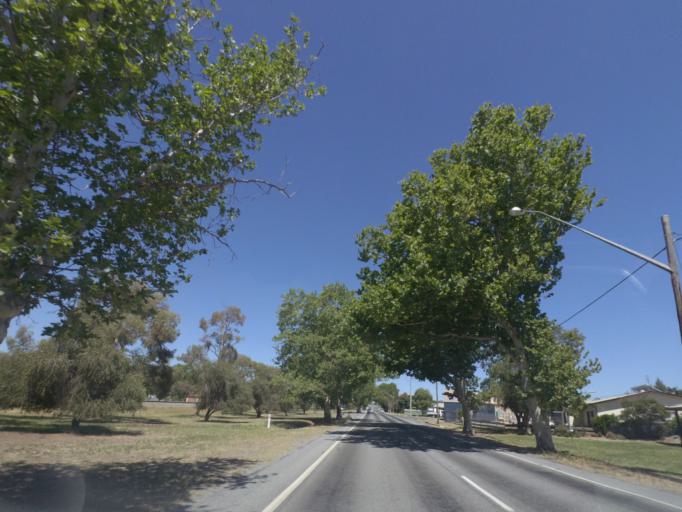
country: AU
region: New South Wales
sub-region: Narrandera
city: Narrandera
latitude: -34.7397
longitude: 146.5647
